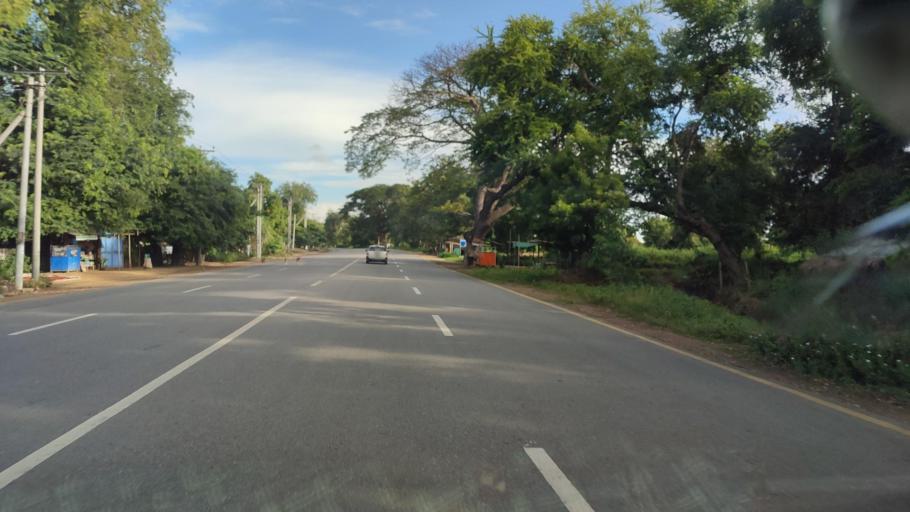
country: MM
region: Mandalay
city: Yamethin
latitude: 20.1885
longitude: 96.1856
